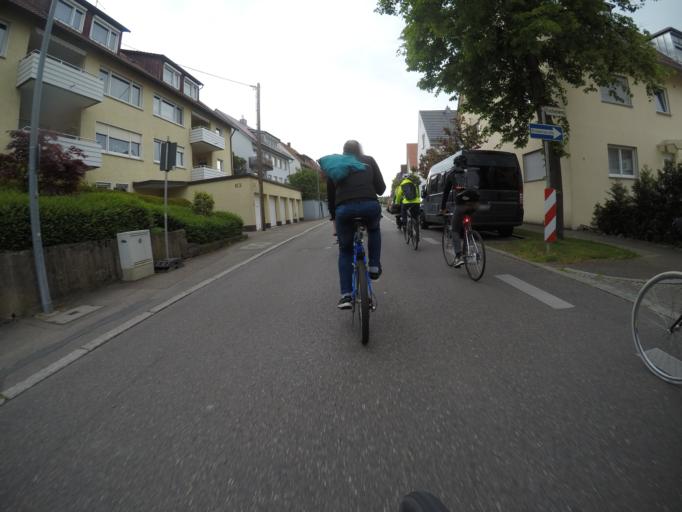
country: DE
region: Baden-Wuerttemberg
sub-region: Regierungsbezirk Stuttgart
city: Esslingen
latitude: 48.7386
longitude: 9.3219
